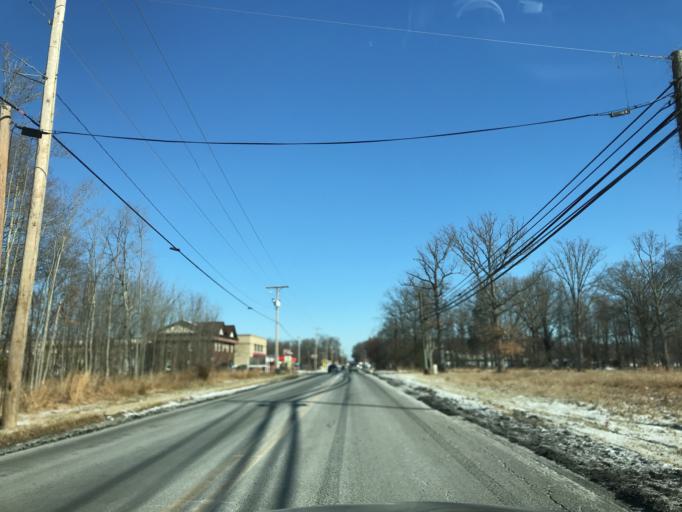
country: US
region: Maryland
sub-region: Charles County
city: Waldorf
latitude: 38.6401
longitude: -76.8926
